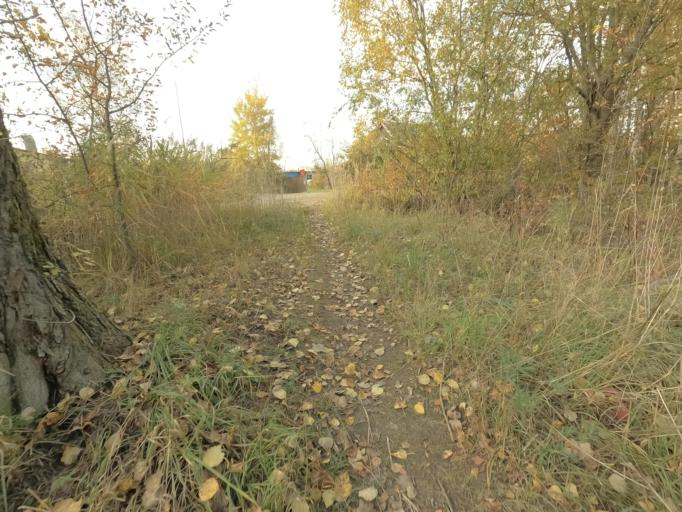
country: RU
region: Leningrad
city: Mga
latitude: 59.7506
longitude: 31.0756
